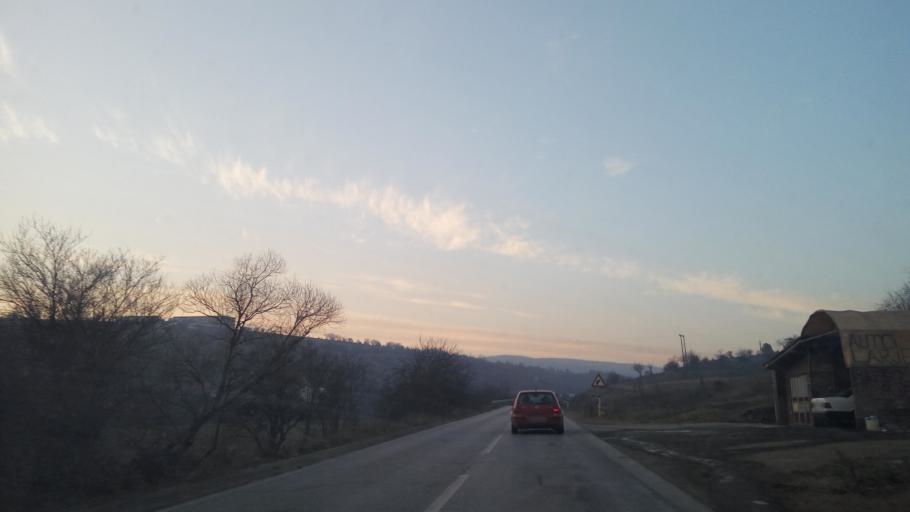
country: XK
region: Gjilan
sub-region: Komuna e Gjilanit
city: Gjilan
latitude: 42.4905
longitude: 21.3924
